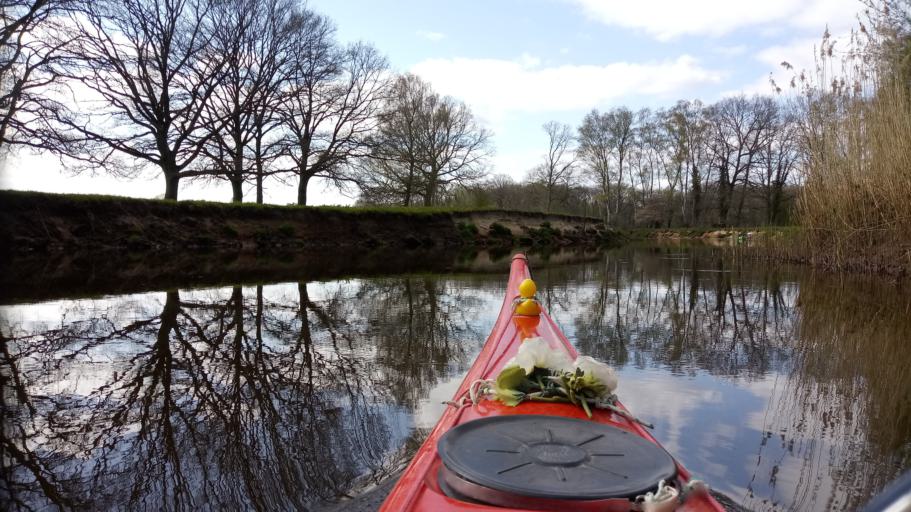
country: NL
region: Overijssel
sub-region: Gemeente Twenterand
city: Den Ham
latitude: 52.4820
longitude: 6.4367
